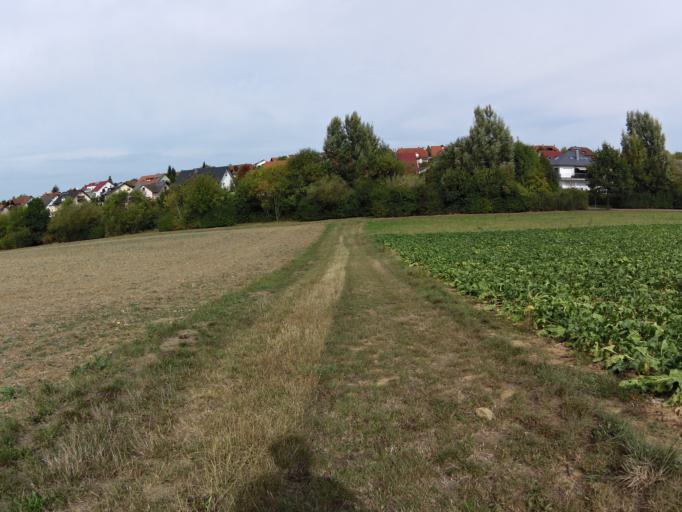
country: DE
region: Bavaria
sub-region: Regierungsbezirk Unterfranken
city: Waldbuttelbrunn
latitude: 49.7818
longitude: 9.8355
